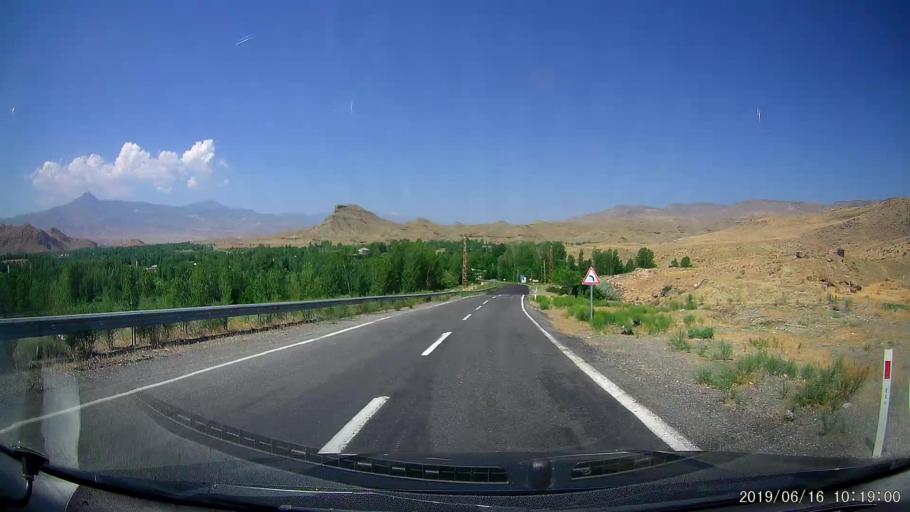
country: TR
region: Igdir
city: Tuzluca
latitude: 40.1562
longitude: 43.6614
